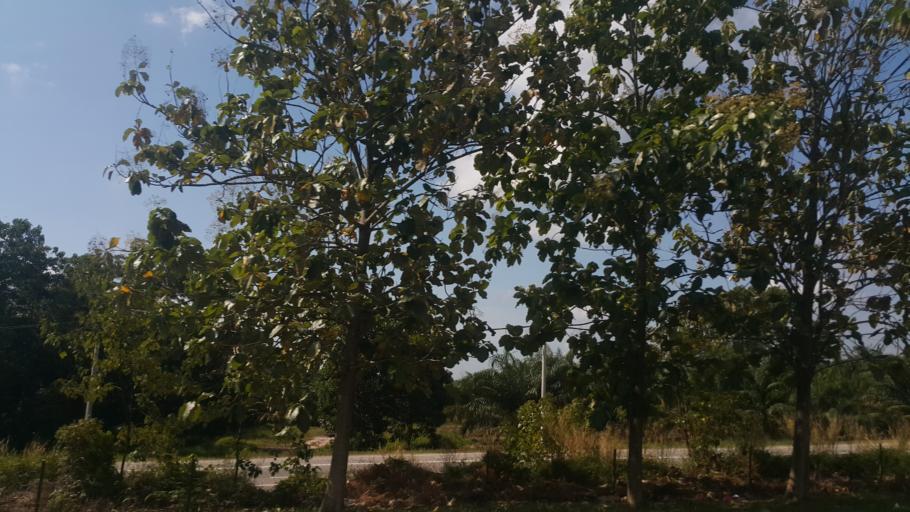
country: MY
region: Johor
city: Yong Peng
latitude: 1.9684
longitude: 103.1203
